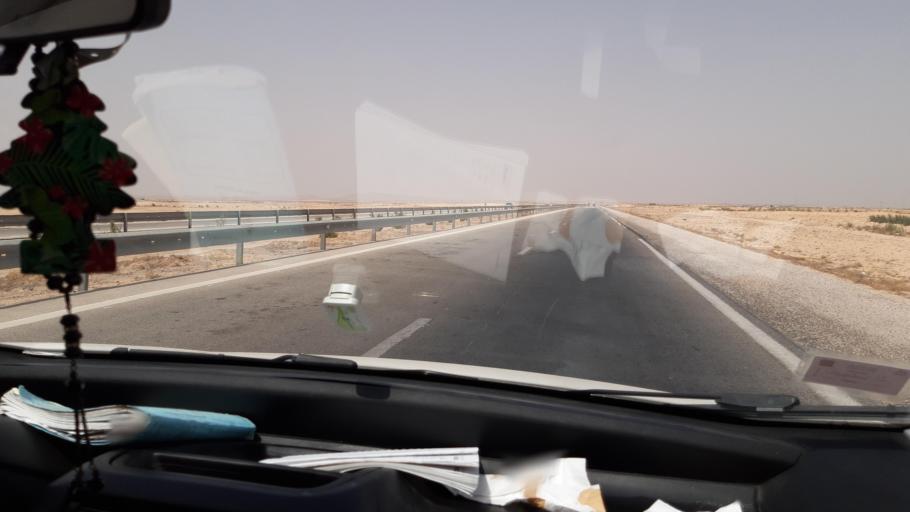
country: TN
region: Qabis
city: Gabes
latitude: 33.9448
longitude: 9.9601
